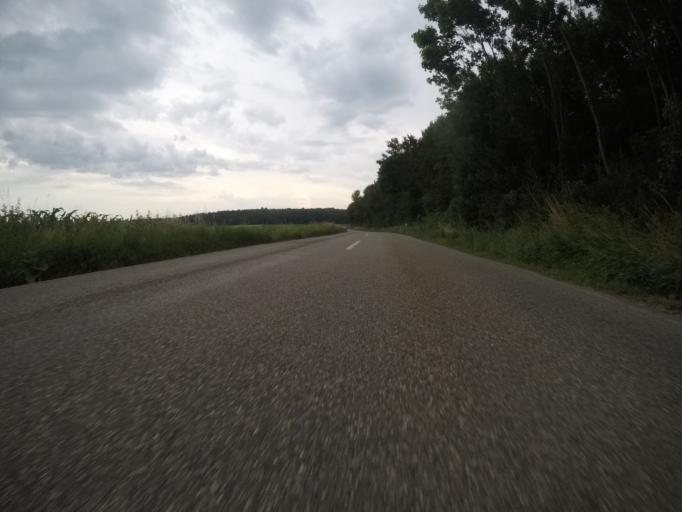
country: DE
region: Baden-Wuerttemberg
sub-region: Regierungsbezirk Stuttgart
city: Eberdingen
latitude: 48.8705
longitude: 8.9929
